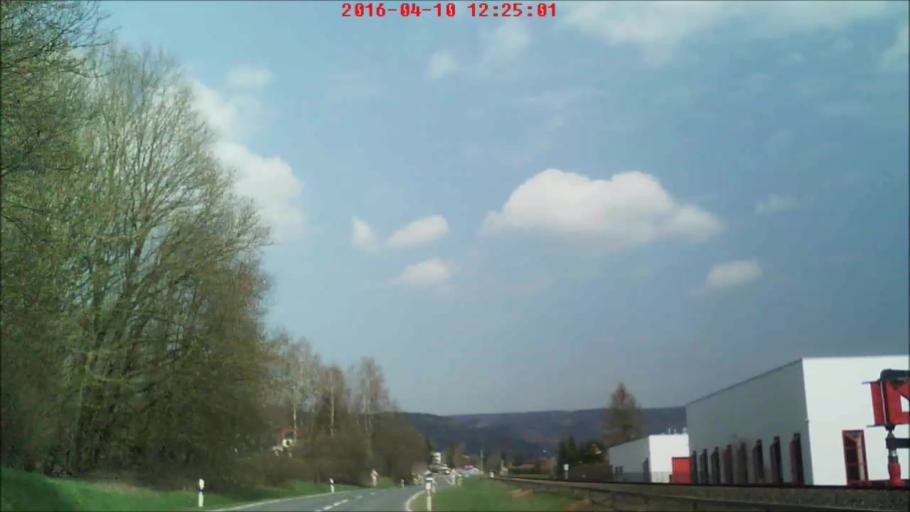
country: DE
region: Thuringia
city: Viernau
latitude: 50.6758
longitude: 10.5522
